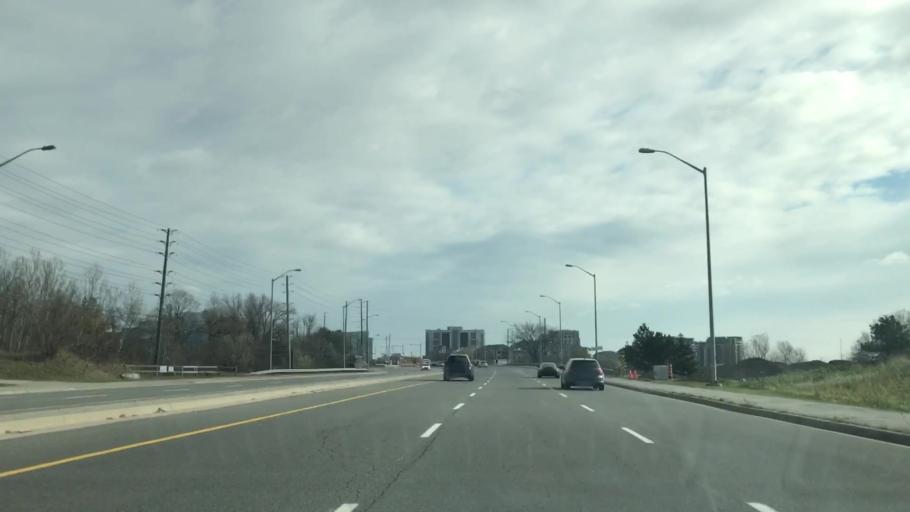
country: CA
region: Ontario
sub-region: York
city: Richmond Hill
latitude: 43.8400
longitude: -79.4038
